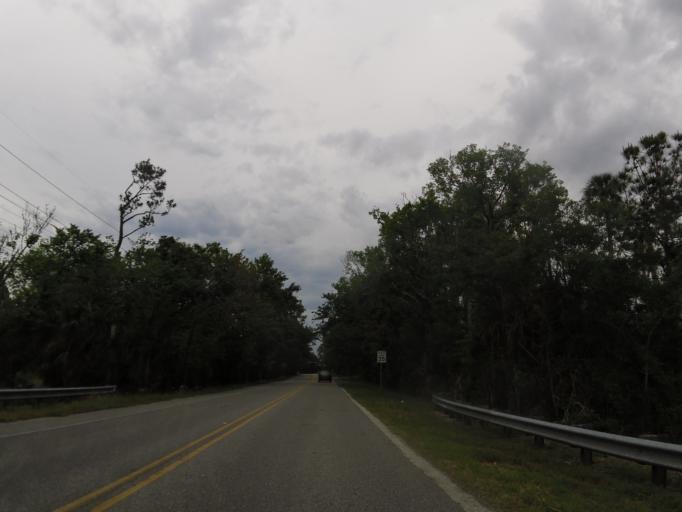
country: US
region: Florida
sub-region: Saint Johns County
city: Ponte Vedra Beach
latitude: 30.2194
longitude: -81.3992
